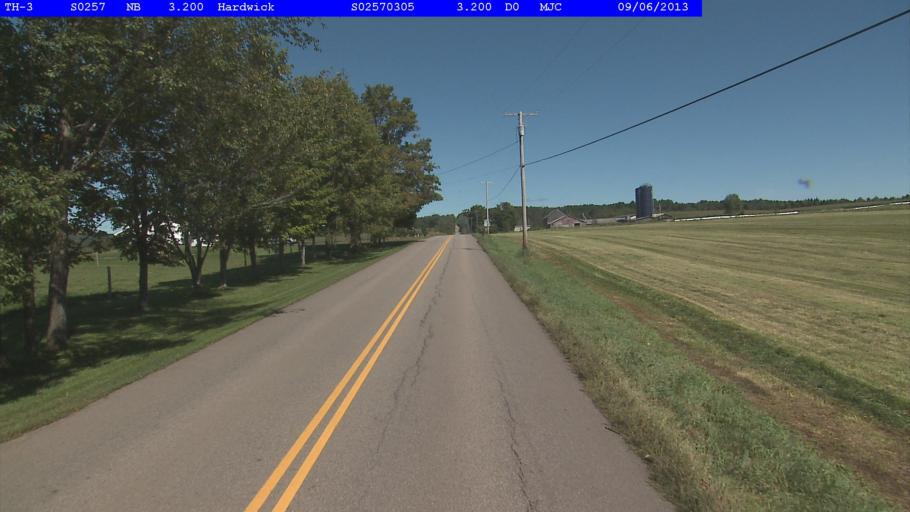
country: US
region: Vermont
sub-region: Caledonia County
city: Hardwick
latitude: 44.5356
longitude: -72.3316
